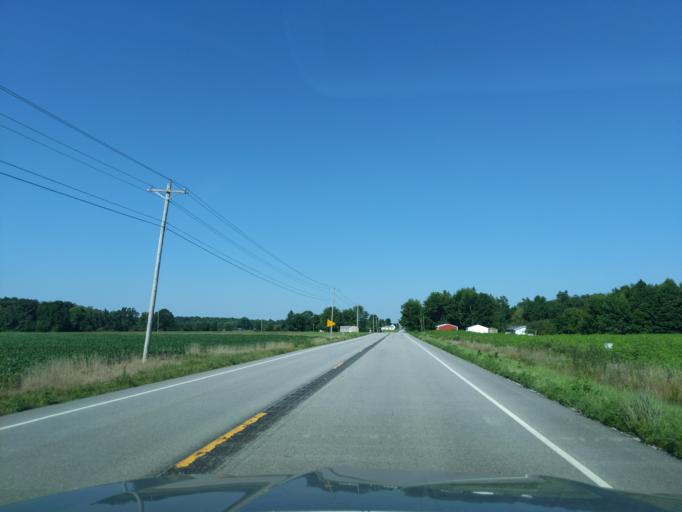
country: US
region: Indiana
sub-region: Ripley County
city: Versailles
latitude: 39.0748
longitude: -85.3026
